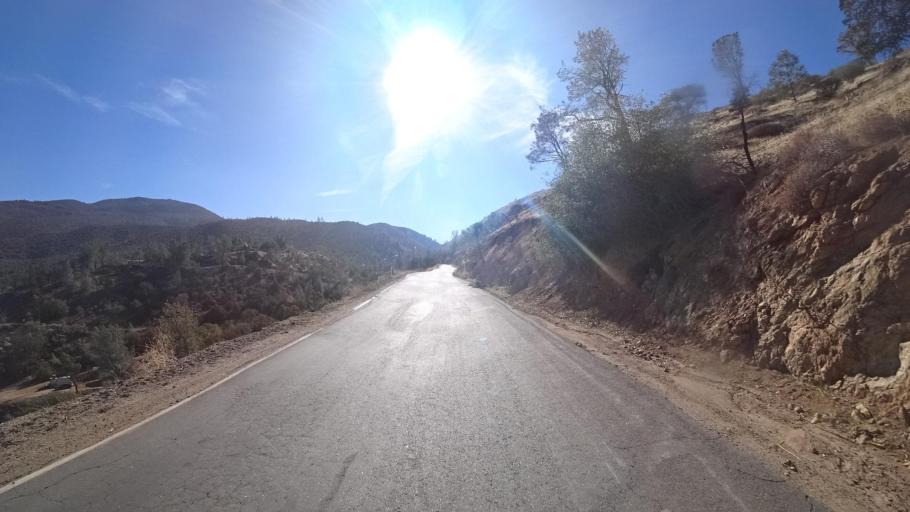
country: US
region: California
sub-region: Kern County
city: Bodfish
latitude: 35.5844
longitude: -118.5015
